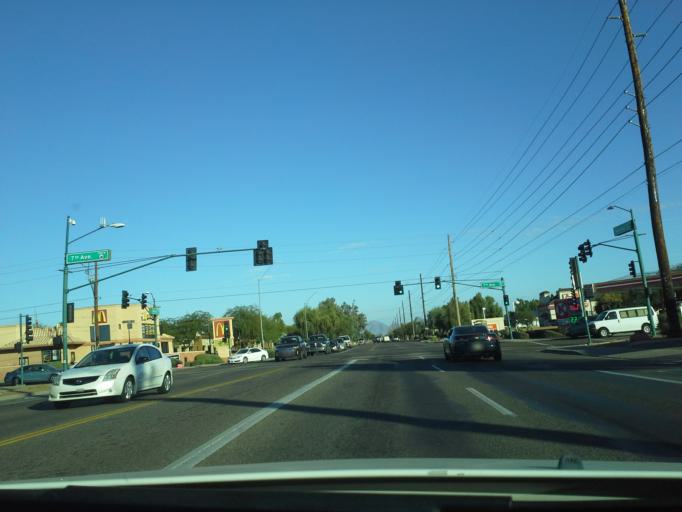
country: US
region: Arizona
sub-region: Maricopa County
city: Glendale
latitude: 33.6546
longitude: -112.0835
